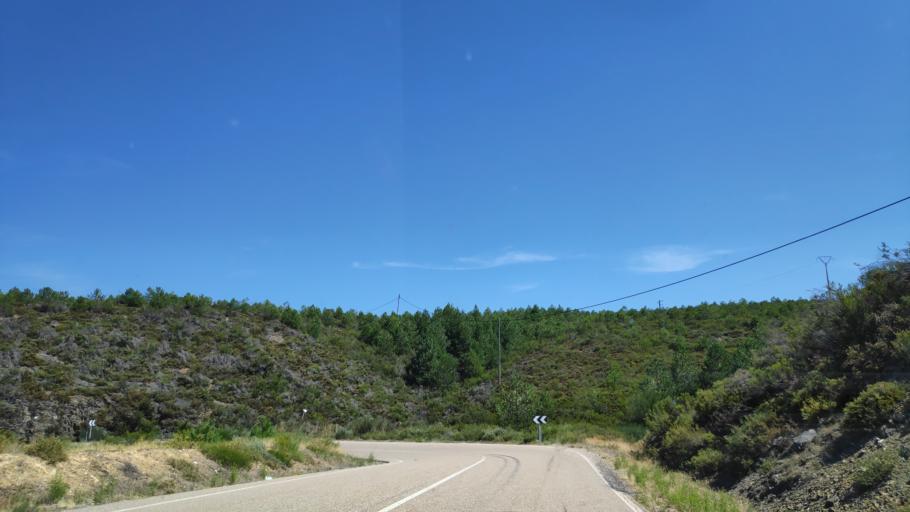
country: ES
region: Castille and Leon
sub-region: Provincia de Zamora
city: Requejo
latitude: 42.0141
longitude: -6.6921
